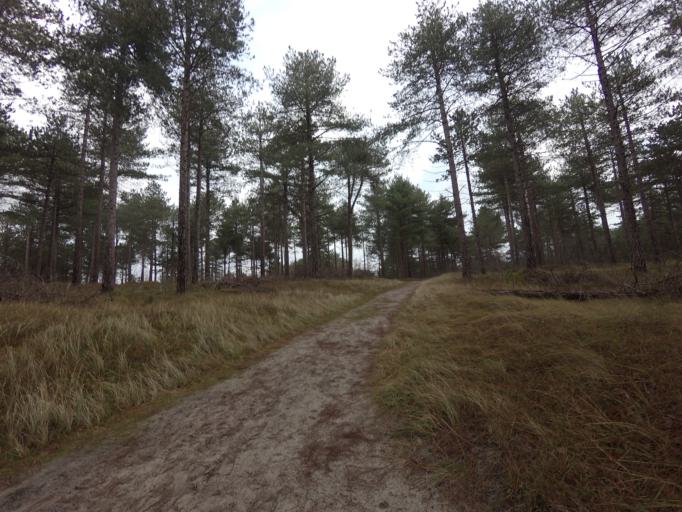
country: NL
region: Zeeland
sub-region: Schouwen-Duiveland
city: Burgh
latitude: 51.6842
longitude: 3.7028
